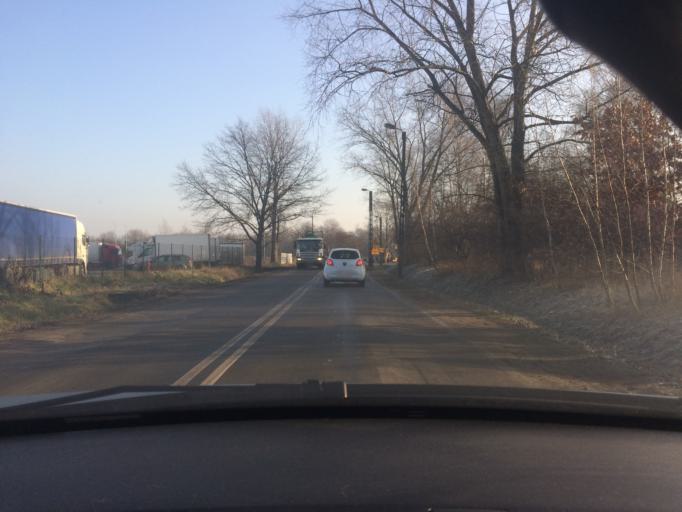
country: PL
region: Lesser Poland Voivodeship
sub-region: Powiat wielicki
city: Czarnochowice
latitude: 50.0229
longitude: 20.0401
